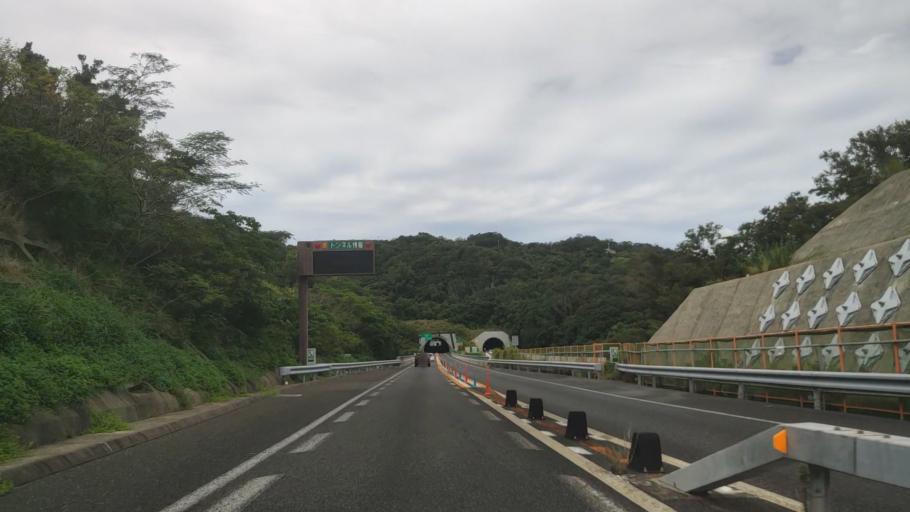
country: JP
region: Wakayama
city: Gobo
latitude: 33.8157
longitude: 135.2289
